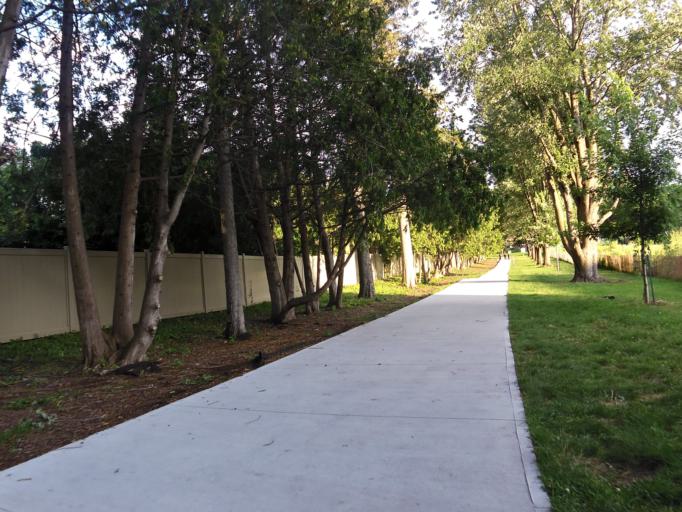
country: CA
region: Ontario
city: Ottawa
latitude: 45.3956
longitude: -75.7430
